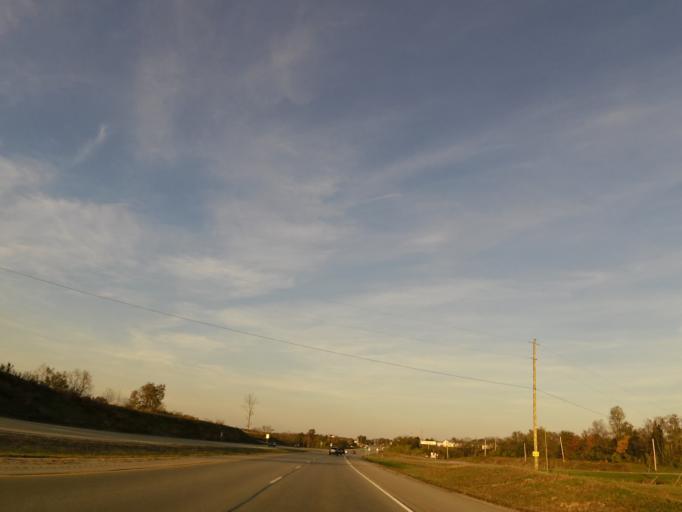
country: US
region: Kentucky
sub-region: Jessamine County
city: Wilmore
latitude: 37.7441
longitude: -84.6286
